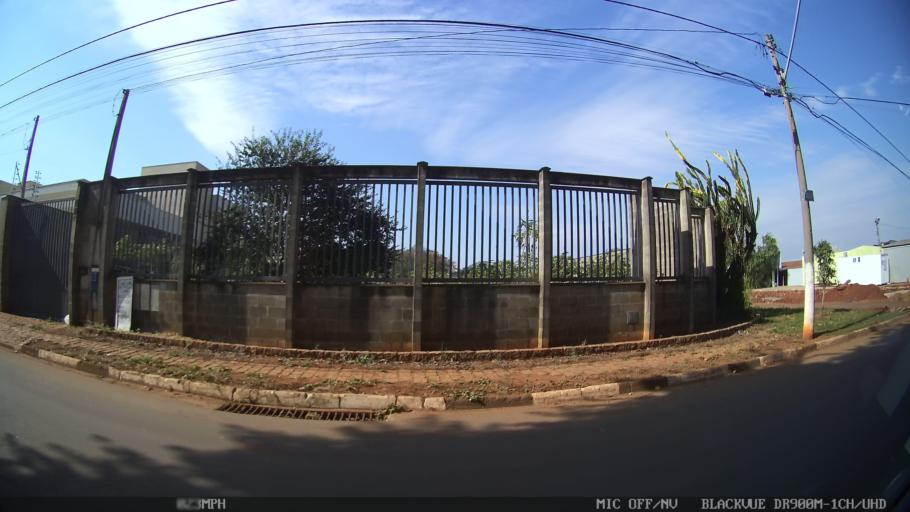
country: BR
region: Sao Paulo
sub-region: Paulinia
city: Paulinia
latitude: -22.7809
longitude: -47.1365
